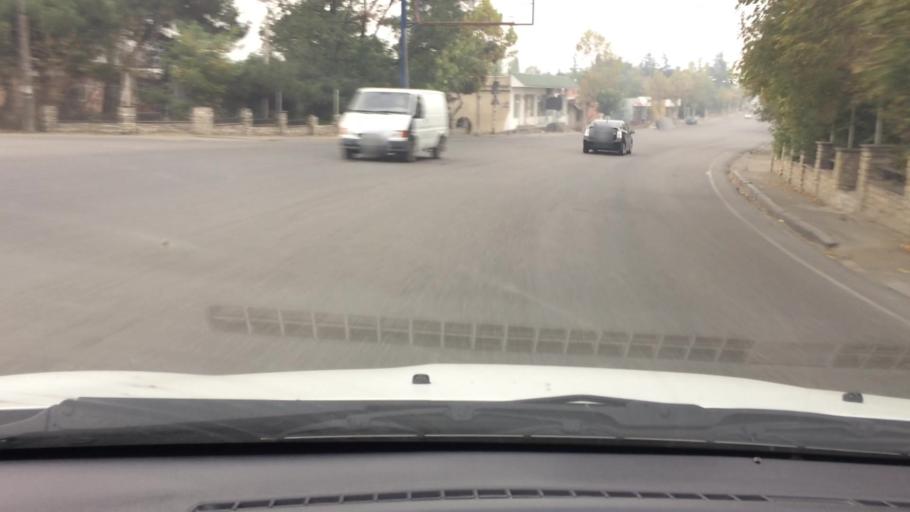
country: GE
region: Kvemo Kartli
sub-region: Marneuli
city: Marneuli
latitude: 41.4919
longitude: 44.8025
